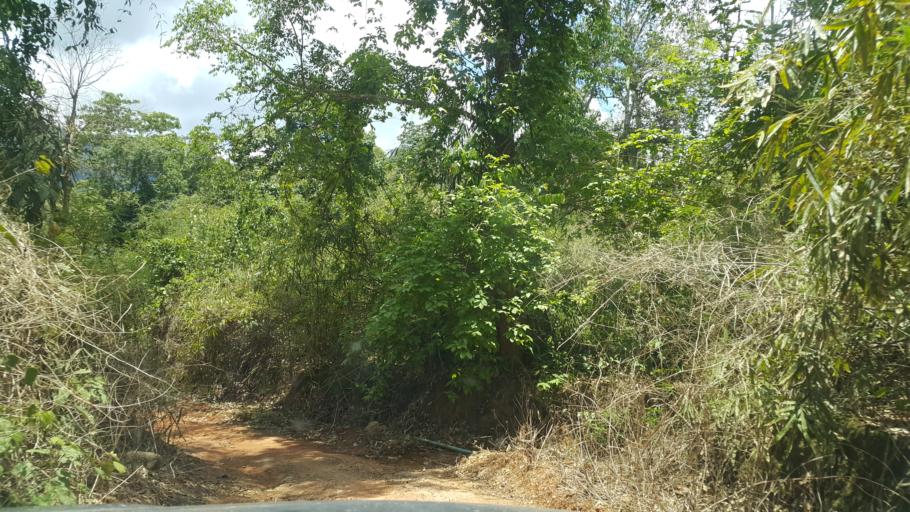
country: TH
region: Phayao
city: Phayao
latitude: 19.1812
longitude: 99.7730
